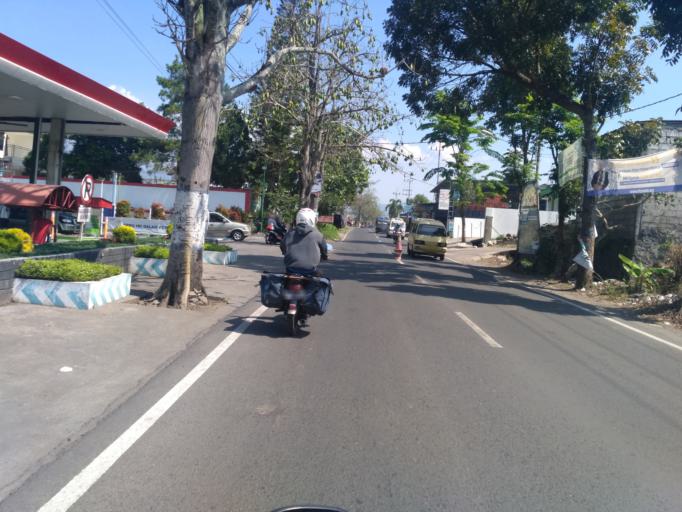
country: ID
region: East Java
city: Batu
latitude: -7.8647
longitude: 112.5425
